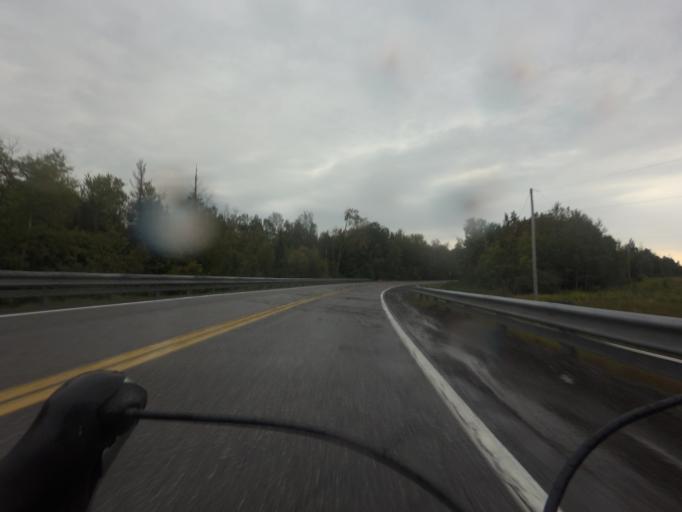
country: CA
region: Ontario
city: Bells Corners
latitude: 45.1963
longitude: -75.7222
